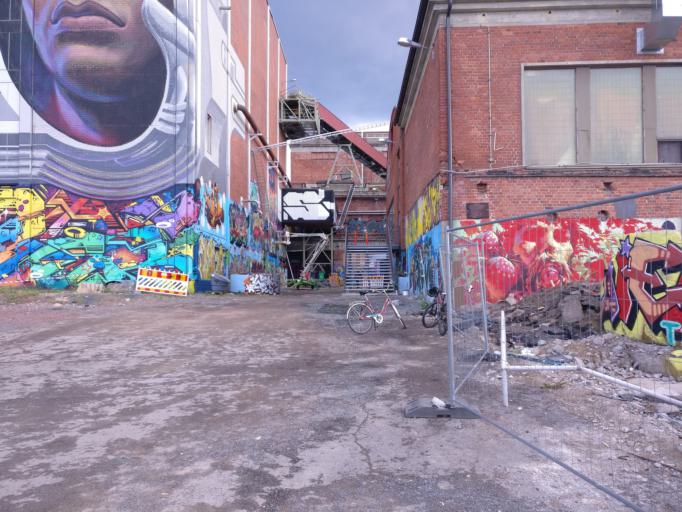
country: FI
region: Pirkanmaa
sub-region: Tampere
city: Pirkkala
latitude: 61.5174
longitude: 23.6841
